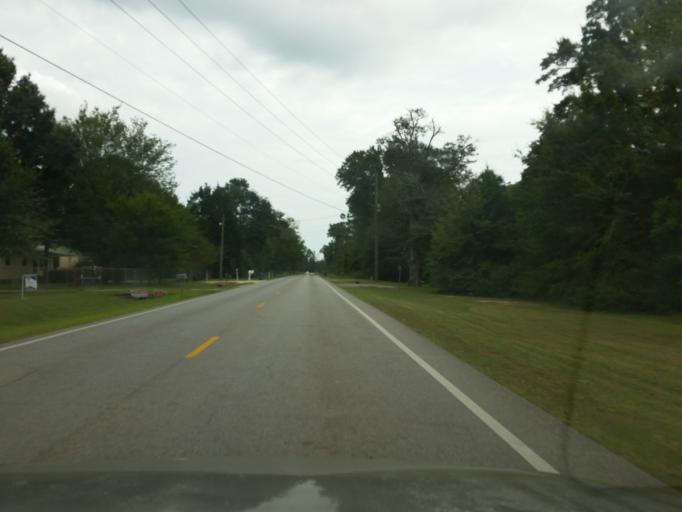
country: US
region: Florida
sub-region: Escambia County
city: Molino
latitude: 30.6835
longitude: -87.3231
